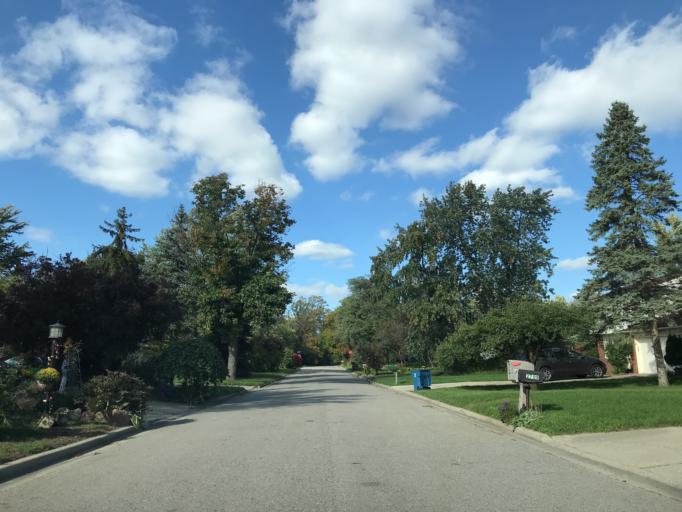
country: US
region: Michigan
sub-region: Washtenaw County
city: Ypsilanti
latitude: 42.2478
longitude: -83.6718
